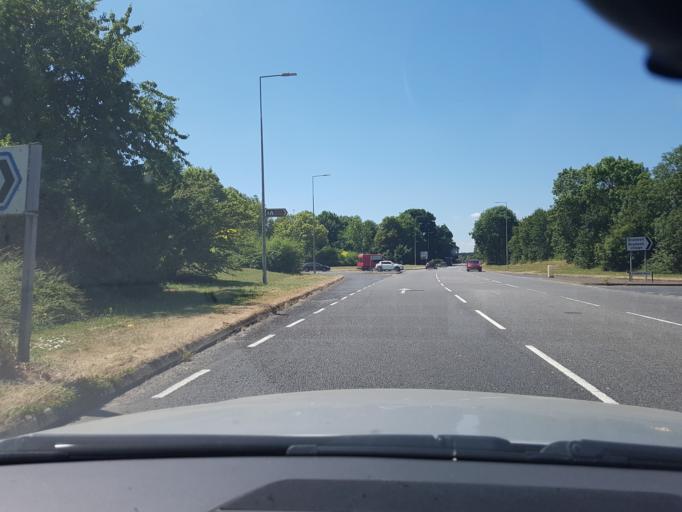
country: GB
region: England
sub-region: Milton Keynes
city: Bradwell
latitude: 52.0439
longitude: -0.7827
